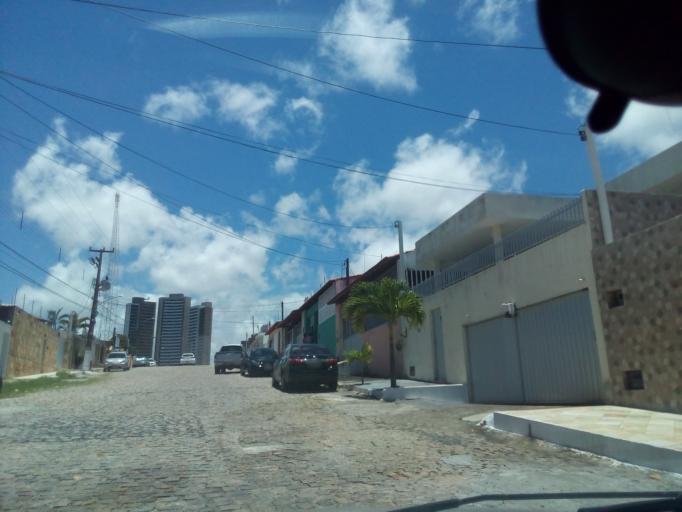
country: BR
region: Rio Grande do Norte
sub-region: Natal
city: Natal
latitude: -5.8449
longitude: -35.2058
